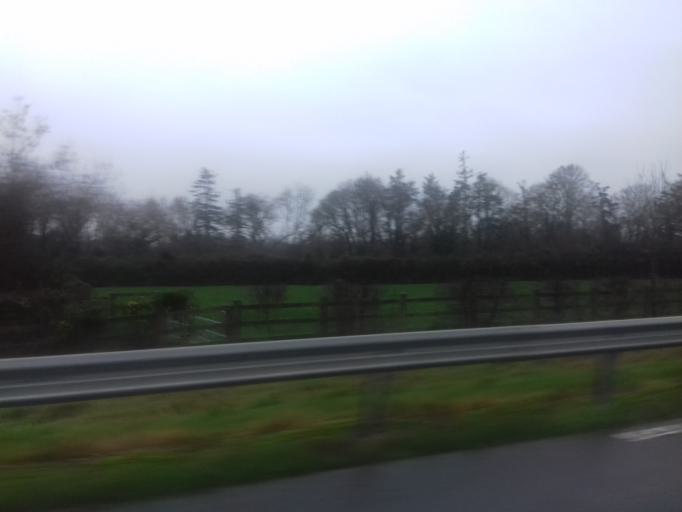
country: IE
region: Leinster
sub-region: County Carlow
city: Bagenalstown
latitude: 52.6898
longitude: -7.0288
